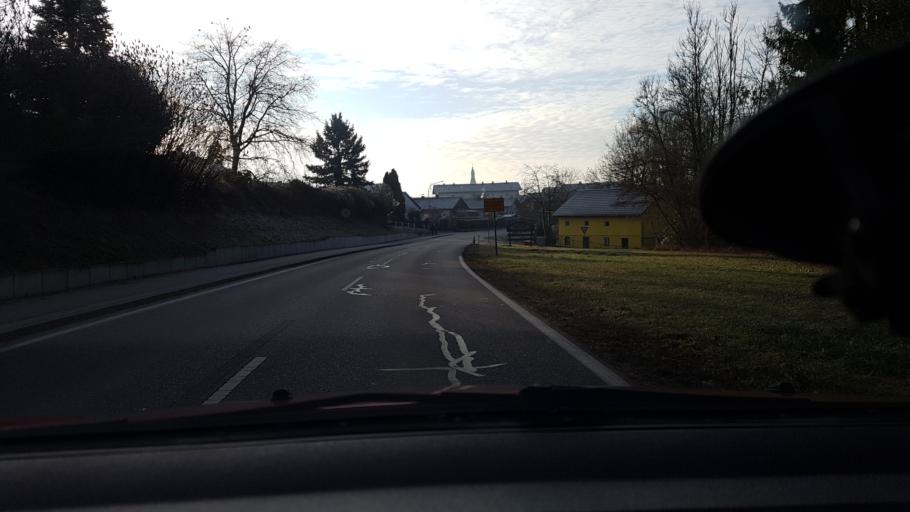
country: DE
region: Bavaria
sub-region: Lower Bavaria
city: Stubenberg
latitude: 48.2938
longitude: 13.0747
